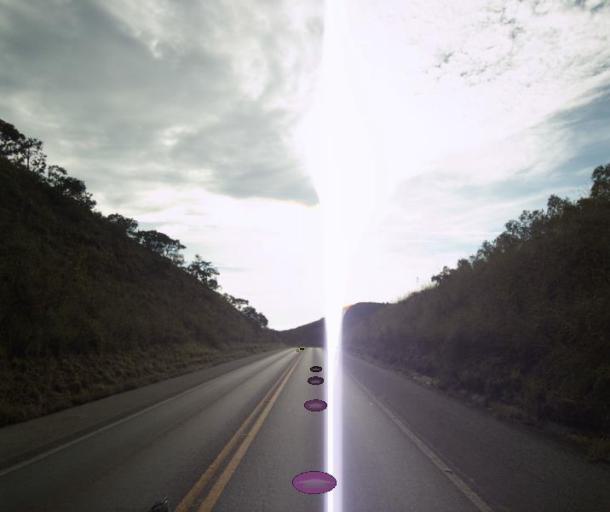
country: BR
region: Goias
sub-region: Pirenopolis
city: Pirenopolis
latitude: -15.7502
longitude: -48.6055
